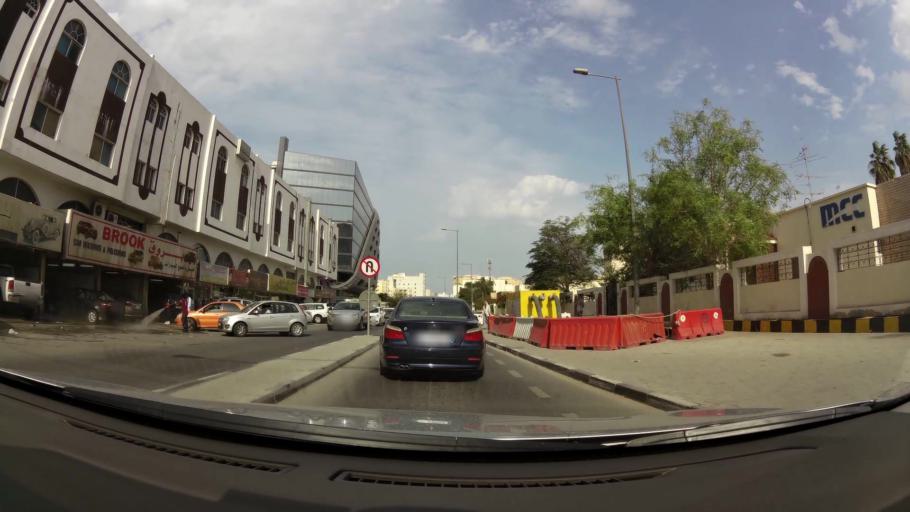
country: QA
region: Baladiyat ad Dawhah
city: Doha
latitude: 25.2795
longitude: 51.5095
